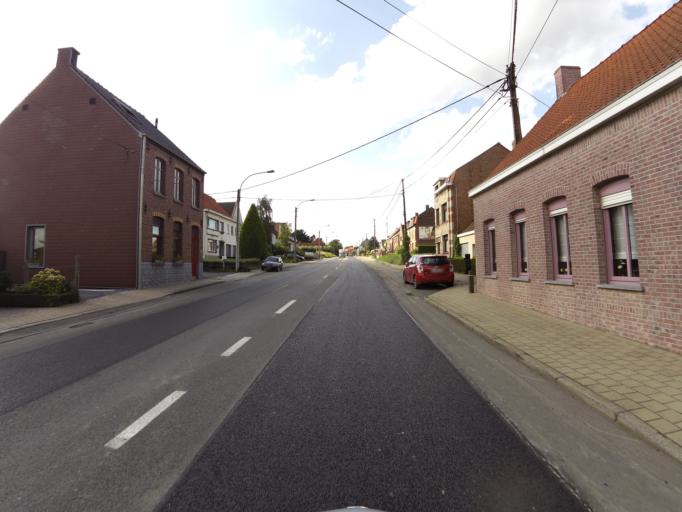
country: BE
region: Flanders
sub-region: Provincie West-Vlaanderen
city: Anzegem
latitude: 50.8306
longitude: 3.4857
